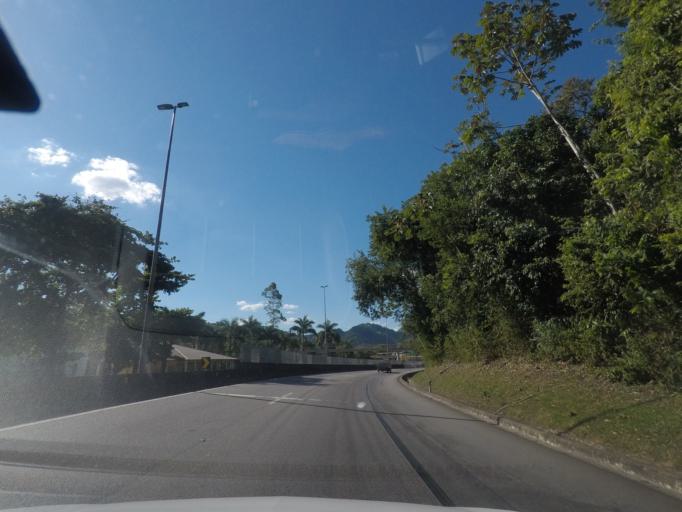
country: BR
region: Rio de Janeiro
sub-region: Petropolis
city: Petropolis
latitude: -22.6629
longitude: -43.1159
